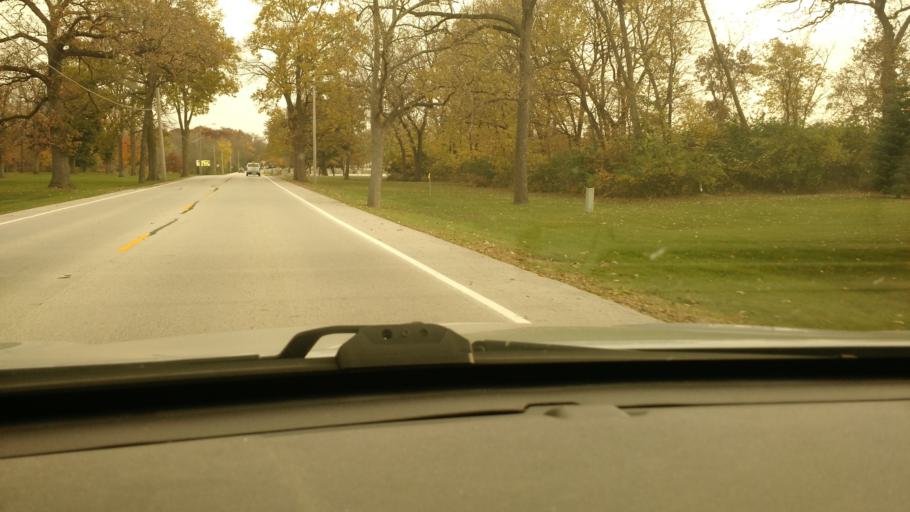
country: US
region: Iowa
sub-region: Scott County
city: Bettendorf
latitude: 41.5163
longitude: -90.5265
